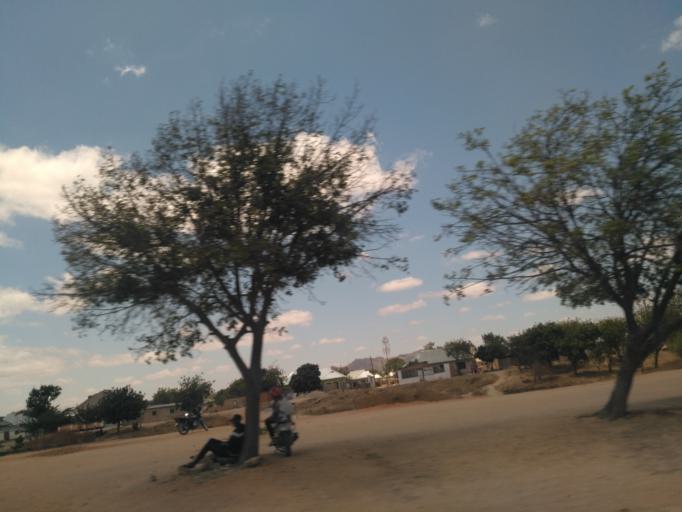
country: TZ
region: Dodoma
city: Kisasa
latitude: -6.1731
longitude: 35.7670
